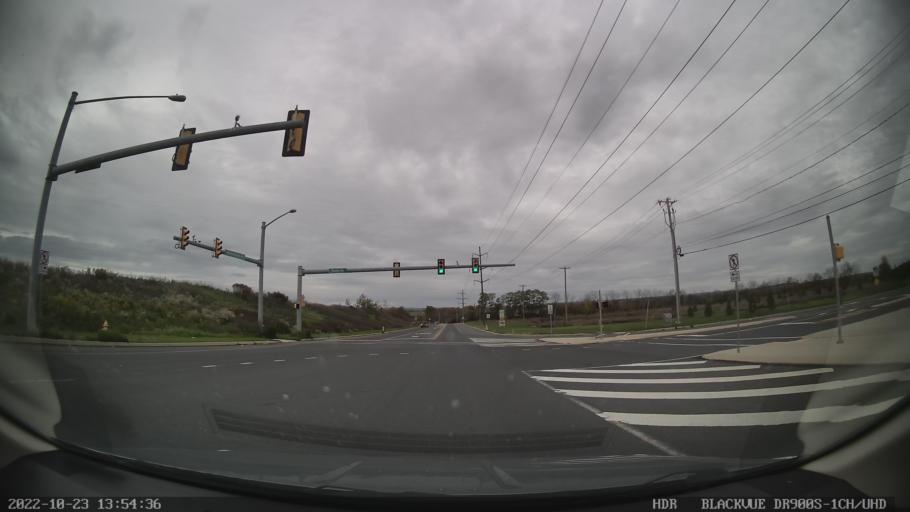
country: US
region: Pennsylvania
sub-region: Northampton County
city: North Catasauqua
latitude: 40.6726
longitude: -75.4590
